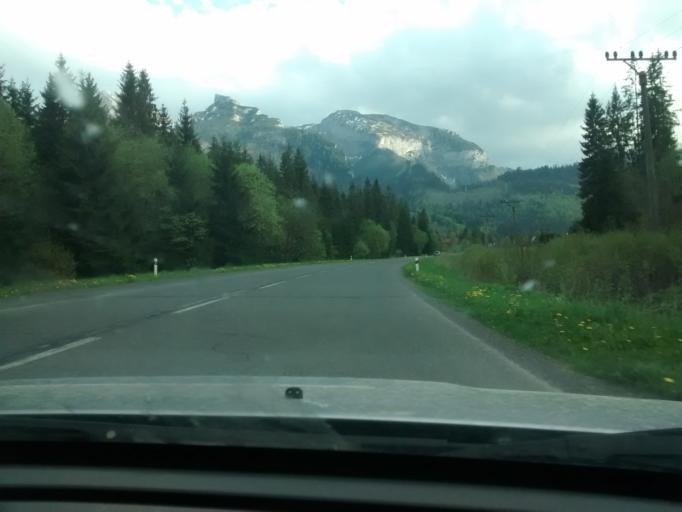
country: PL
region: Lesser Poland Voivodeship
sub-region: Powiat tatrzanski
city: Bukowina Tatrzanska
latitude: 49.2866
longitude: 20.1750
